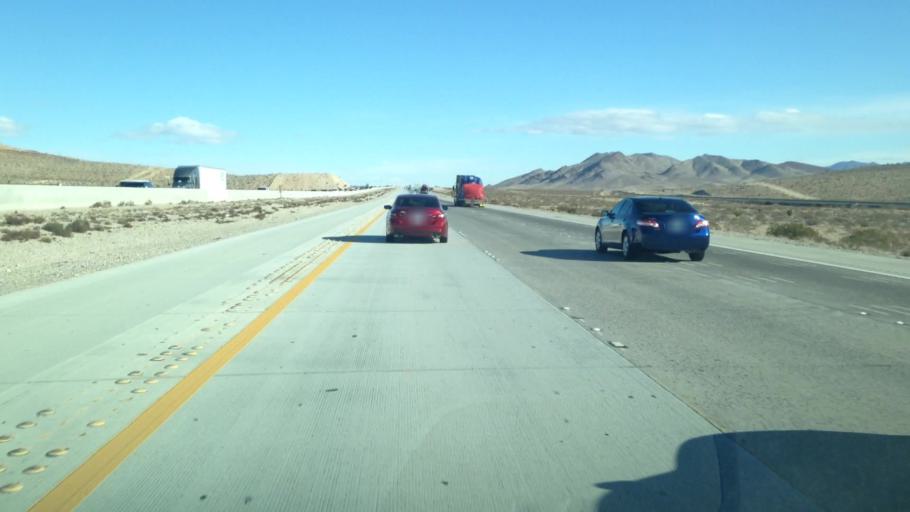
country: US
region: Nevada
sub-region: Clark County
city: Enterprise
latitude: 35.8618
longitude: -115.2533
